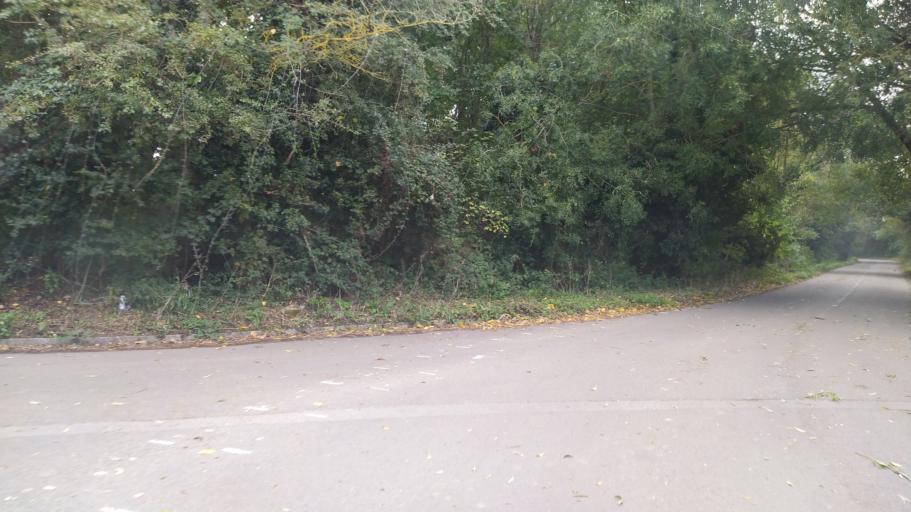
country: GB
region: England
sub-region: West Berkshire
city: Calcot
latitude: 51.4243
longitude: -1.0077
